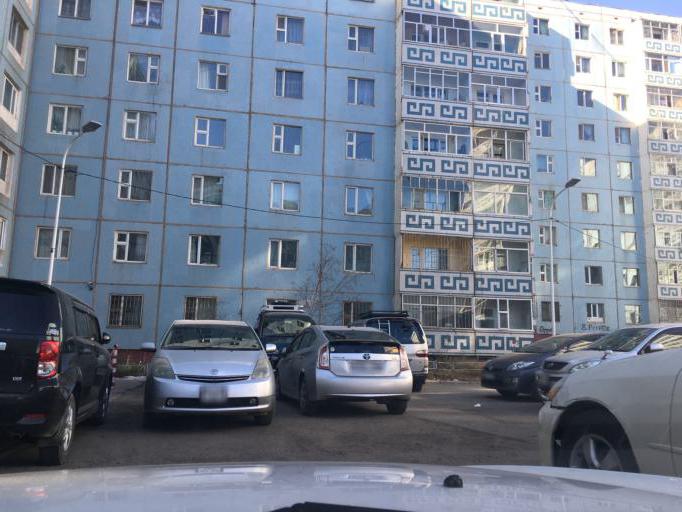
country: MN
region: Ulaanbaatar
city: Ulaanbaatar
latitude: 47.9213
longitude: 106.8692
